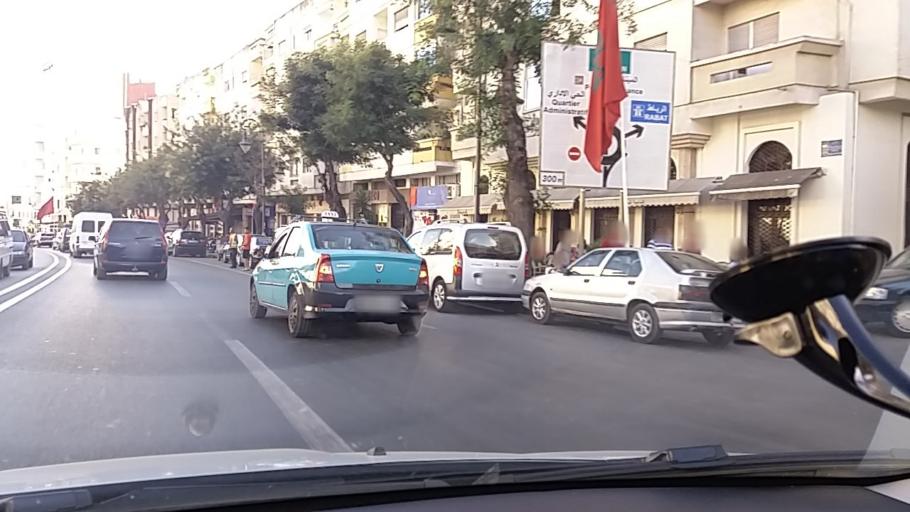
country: MA
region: Tanger-Tetouan
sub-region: Tanger-Assilah
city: Tangier
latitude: 35.7741
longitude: -5.8172
